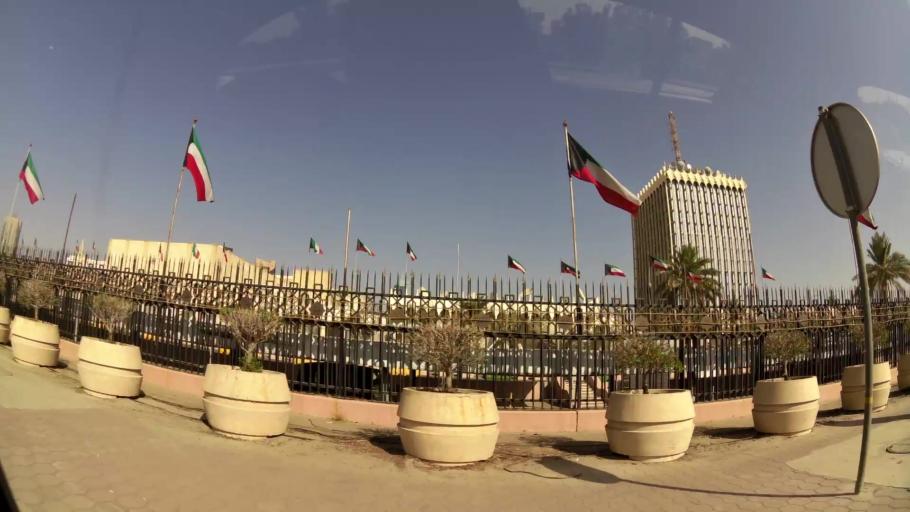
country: KW
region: Al Asimah
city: Kuwait City
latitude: 29.3615
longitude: 47.9718
